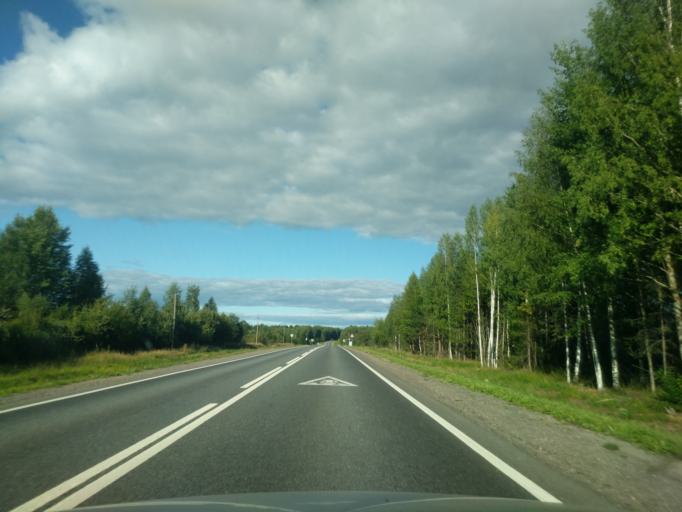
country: RU
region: Kostroma
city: Manturovo
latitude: 58.1600
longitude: 44.3927
